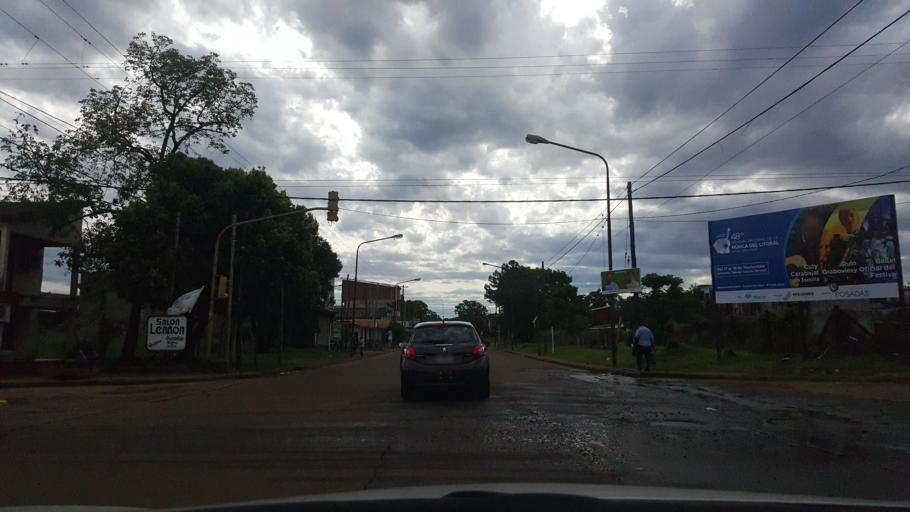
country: AR
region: Misiones
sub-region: Departamento de Capital
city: Posadas
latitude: -27.3706
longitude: -55.9320
